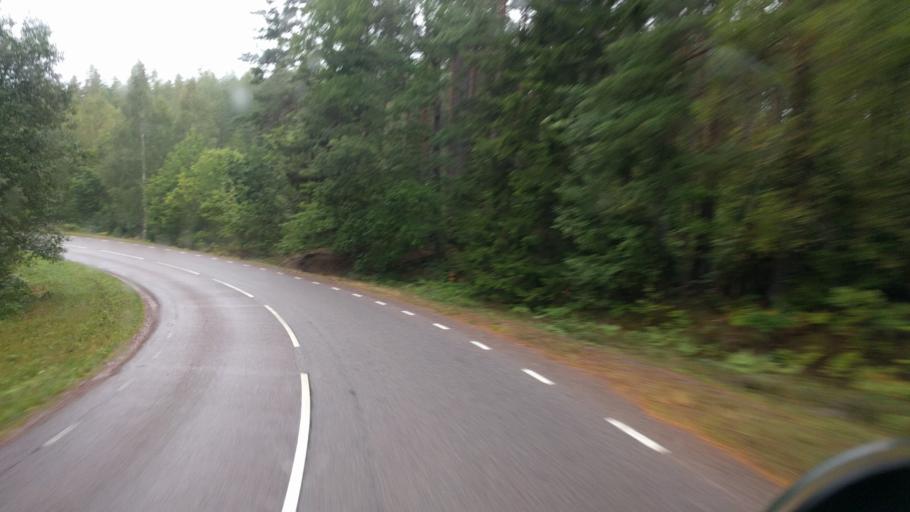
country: SE
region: Kalmar
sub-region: Vasterviks Kommun
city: Gamleby
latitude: 57.8201
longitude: 16.4555
